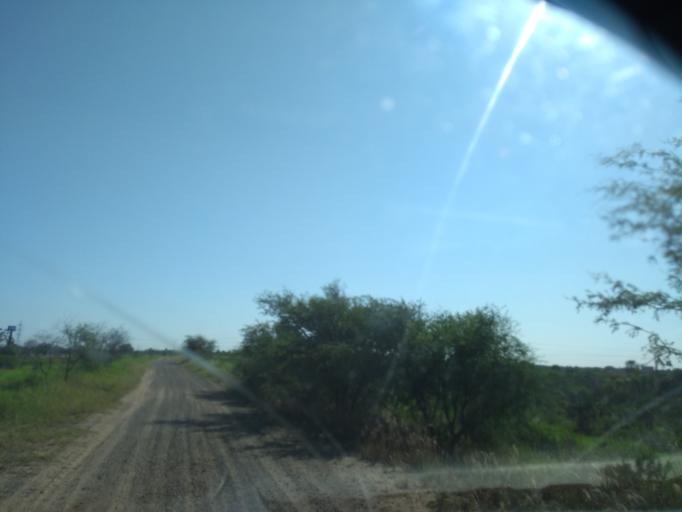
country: AR
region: Chaco
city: Barranqueras
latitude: -27.4431
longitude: -58.8939
